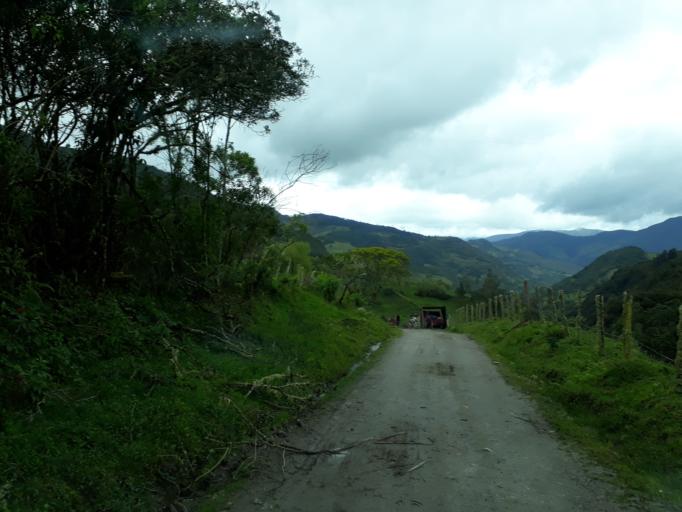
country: CO
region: Cundinamarca
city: Junin
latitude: 4.6778
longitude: -73.6789
